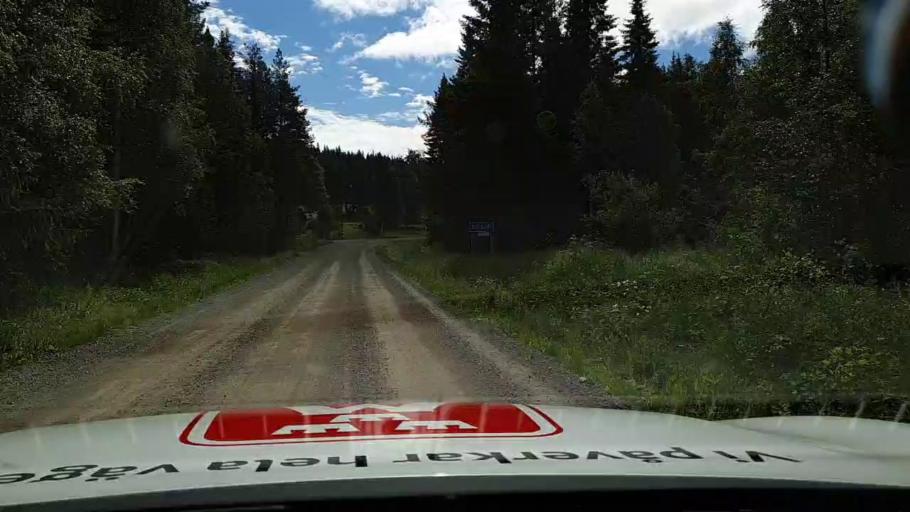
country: SE
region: Jaemtland
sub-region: Braecke Kommun
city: Braecke
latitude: 62.7786
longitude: 15.4767
